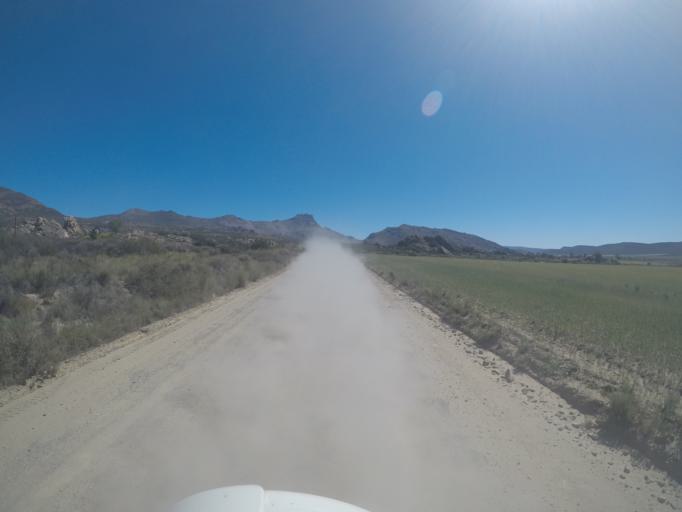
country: ZA
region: Western Cape
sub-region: Cape Winelands District Municipality
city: Ceres
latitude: -32.8790
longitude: 19.4487
